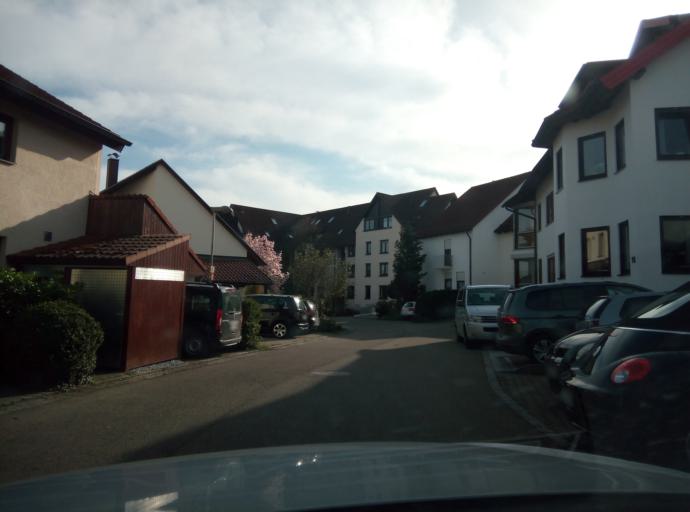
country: DE
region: Baden-Wuerttemberg
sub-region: Tuebingen Region
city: Tuebingen
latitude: 48.5449
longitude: 9.0658
